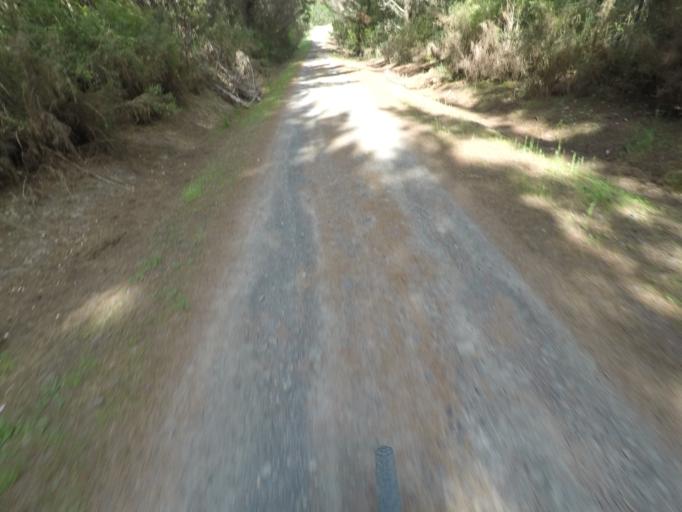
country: NZ
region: Auckland
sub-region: Auckland
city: Muriwai Beach
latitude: -36.7433
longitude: 174.5706
